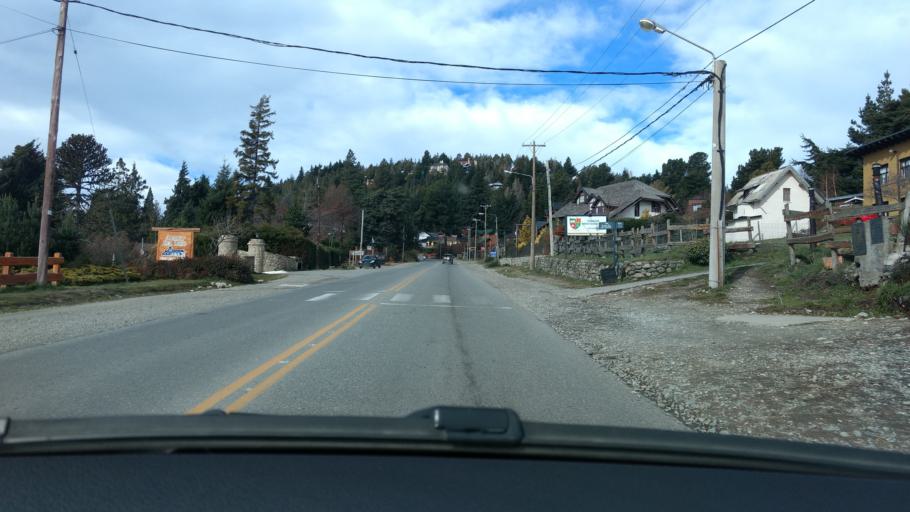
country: AR
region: Rio Negro
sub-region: Departamento de Bariloche
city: San Carlos de Bariloche
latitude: -41.1215
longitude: -71.3959
